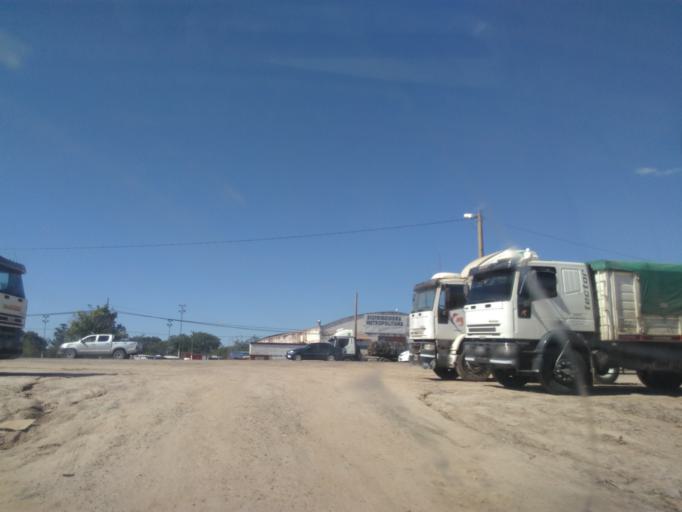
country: AR
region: Chaco
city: Fontana
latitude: -27.4229
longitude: -59.0093
